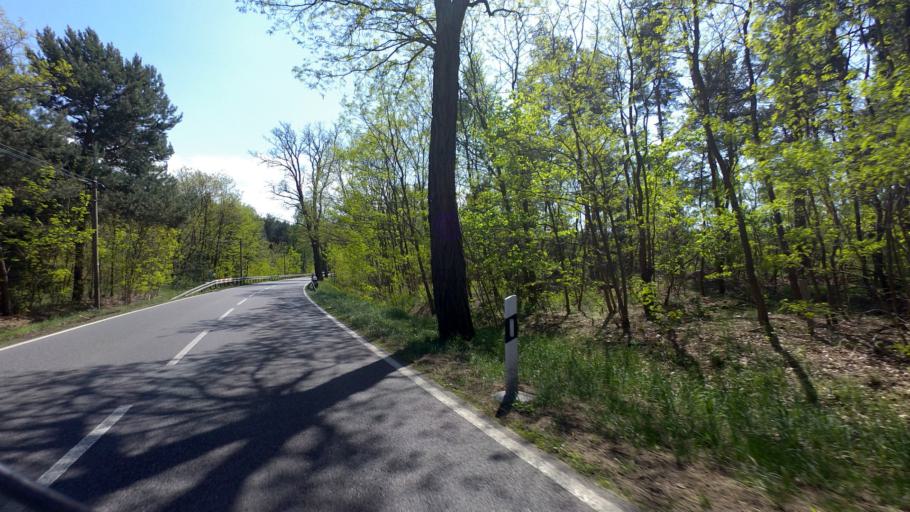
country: DE
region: Brandenburg
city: Lieberose
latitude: 51.9970
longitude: 14.2032
